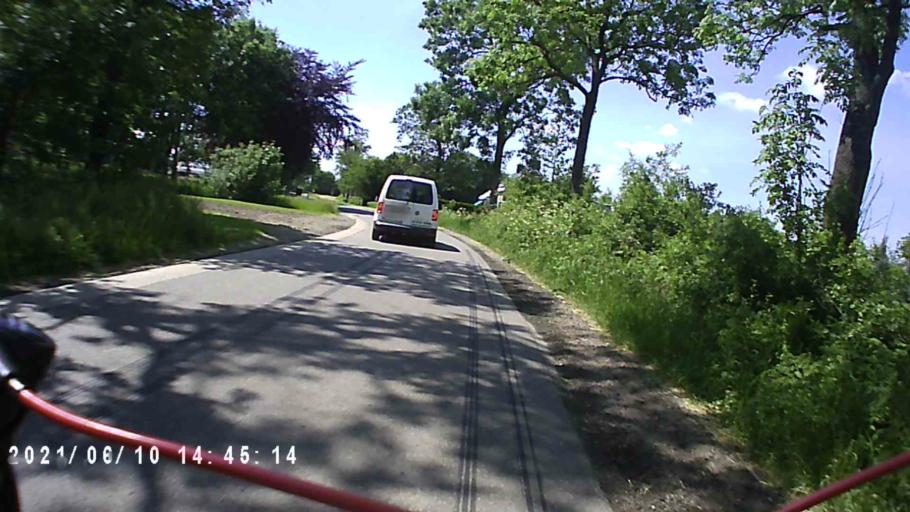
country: NL
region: Groningen
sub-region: Gemeente Grootegast
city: Grootegast
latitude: 53.2369
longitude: 6.2799
